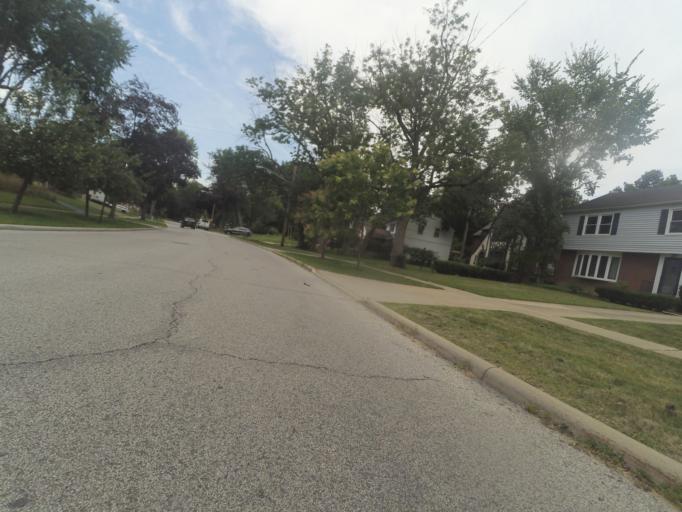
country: US
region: Ohio
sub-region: Cuyahoga County
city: University Heights
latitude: 41.4910
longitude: -81.5423
